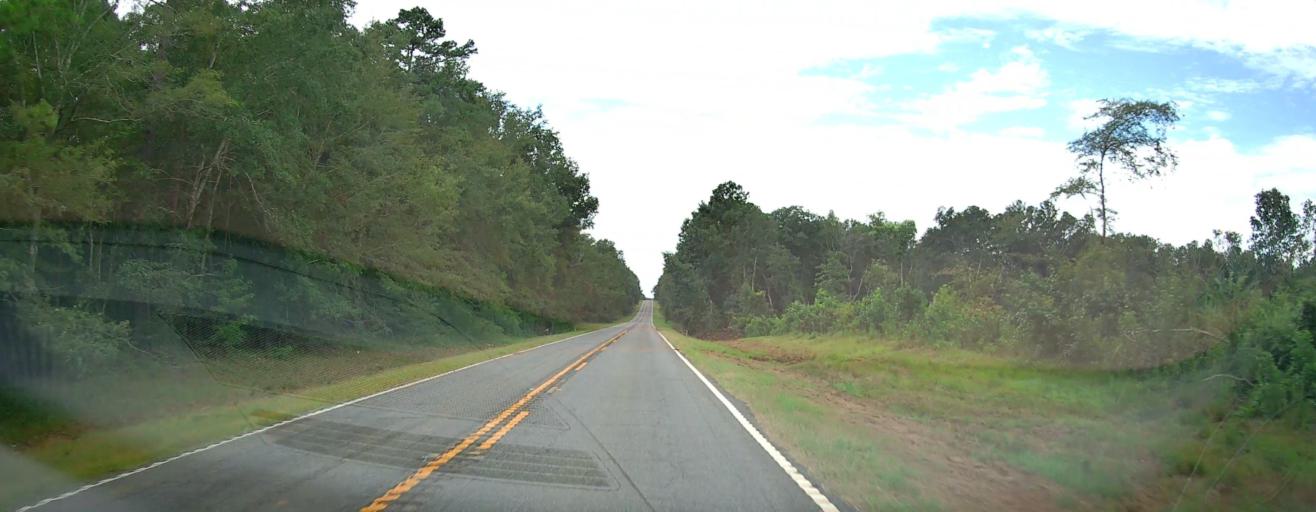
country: US
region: Georgia
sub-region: Dooly County
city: Unadilla
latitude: 32.2909
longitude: -83.8462
